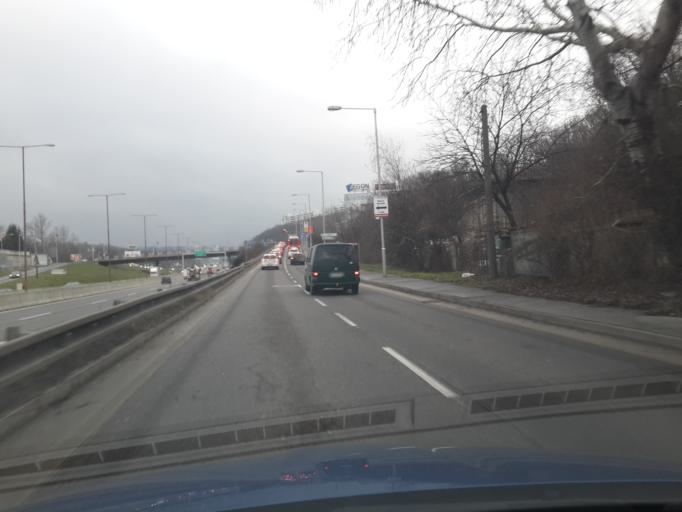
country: SK
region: Bratislavsky
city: Bratislava
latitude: 48.1513
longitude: 17.0766
